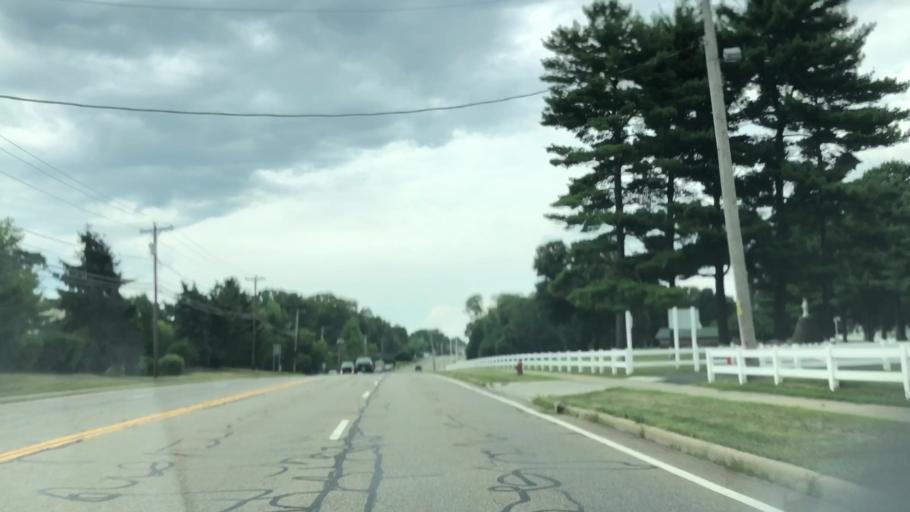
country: US
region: Ohio
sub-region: Summit County
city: Portage Lakes
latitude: 40.9922
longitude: -81.5220
